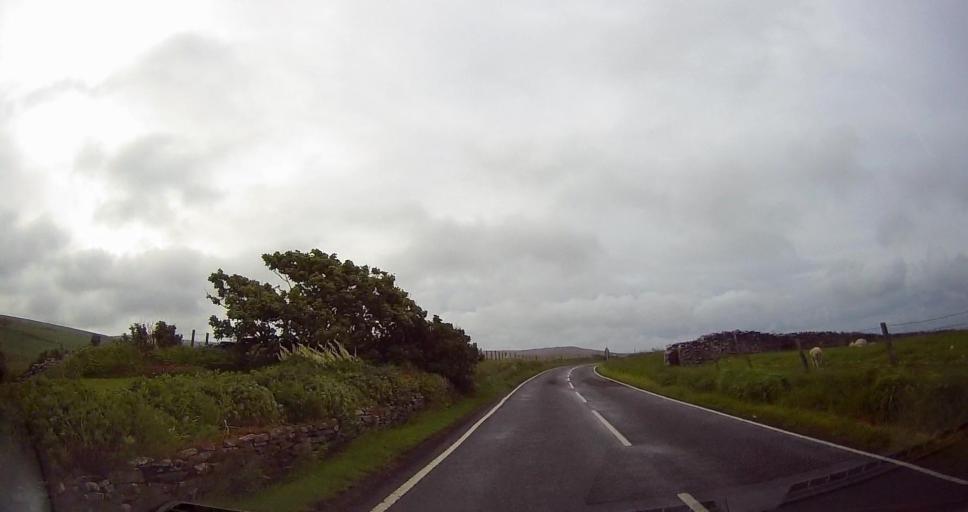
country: GB
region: Scotland
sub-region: Orkney Islands
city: Stromness
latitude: 58.9687
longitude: -3.2287
